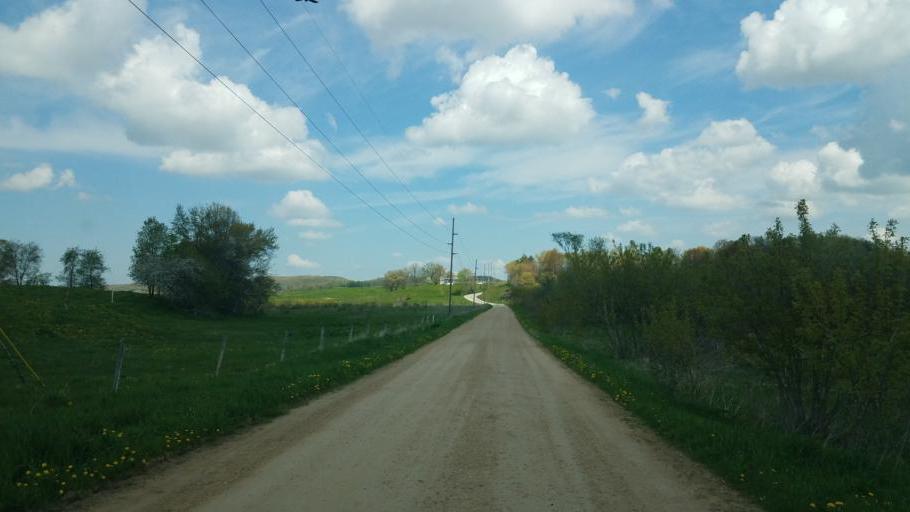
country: US
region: Wisconsin
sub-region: Vernon County
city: Hillsboro
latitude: 43.6782
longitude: -90.3325
